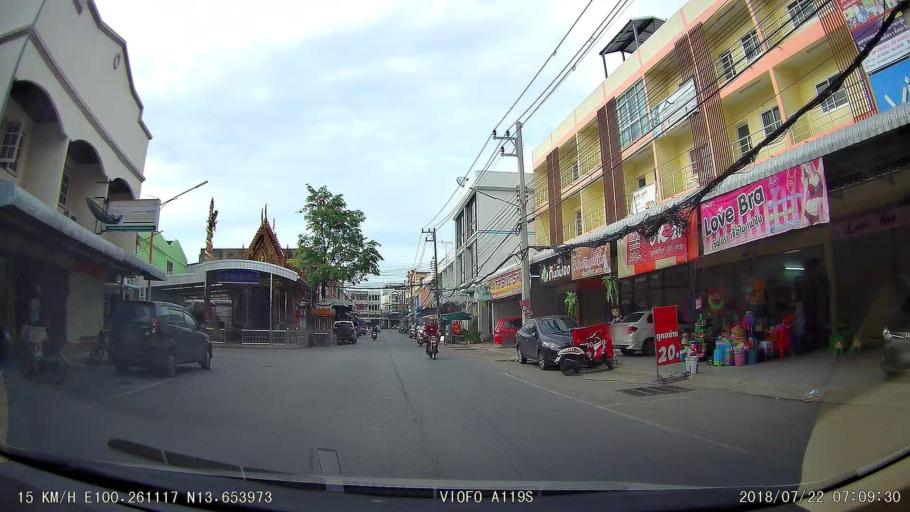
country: TH
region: Samut Sakhon
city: Krathum Baen
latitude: 13.6539
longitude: 100.2612
